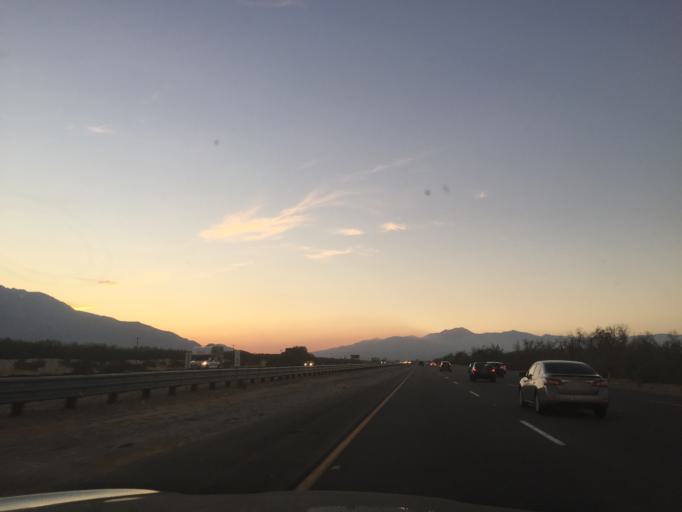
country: US
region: California
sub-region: Riverside County
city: Thousand Palms
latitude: 33.8370
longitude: -116.4374
